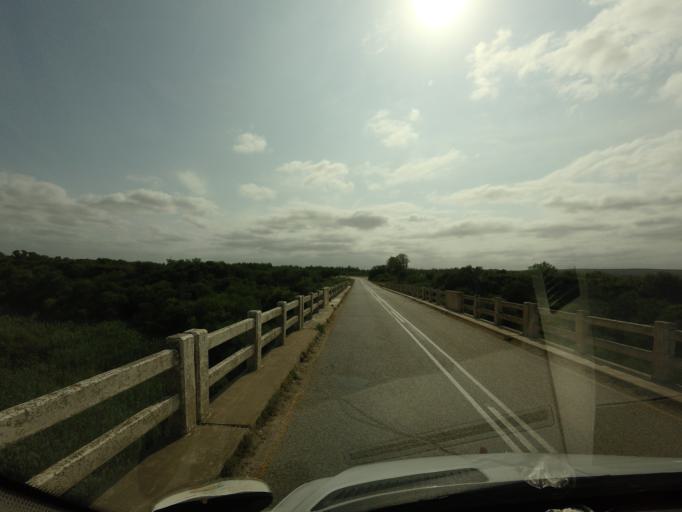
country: ZA
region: Eastern Cape
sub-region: Cacadu District Municipality
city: Kirkwood
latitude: -33.5815
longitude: 25.6742
